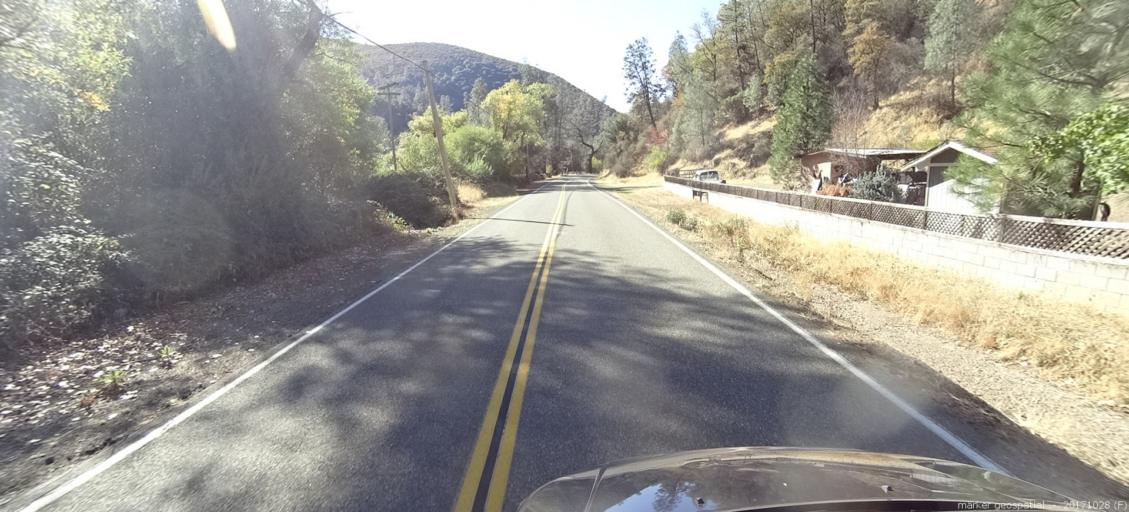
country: US
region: California
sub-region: Trinity County
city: Lewiston
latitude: 40.7208
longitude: -122.6286
